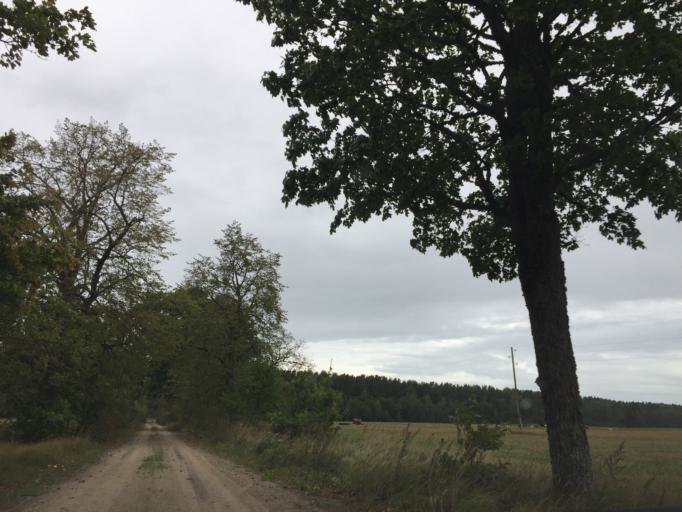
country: LV
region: Salacgrivas
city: Salacgriva
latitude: 57.7032
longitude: 24.3617
